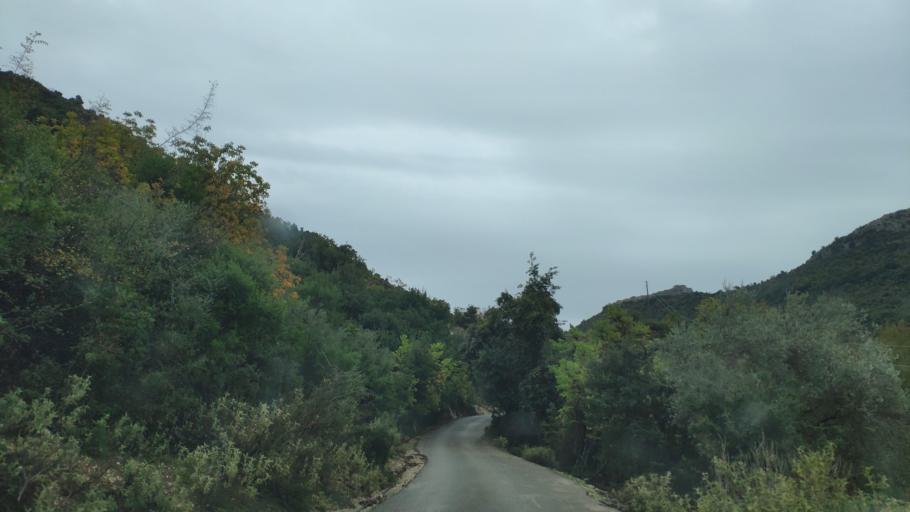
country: GR
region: Epirus
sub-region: Nomos Prevezis
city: Kanalaki
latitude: 39.3447
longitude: 20.6510
